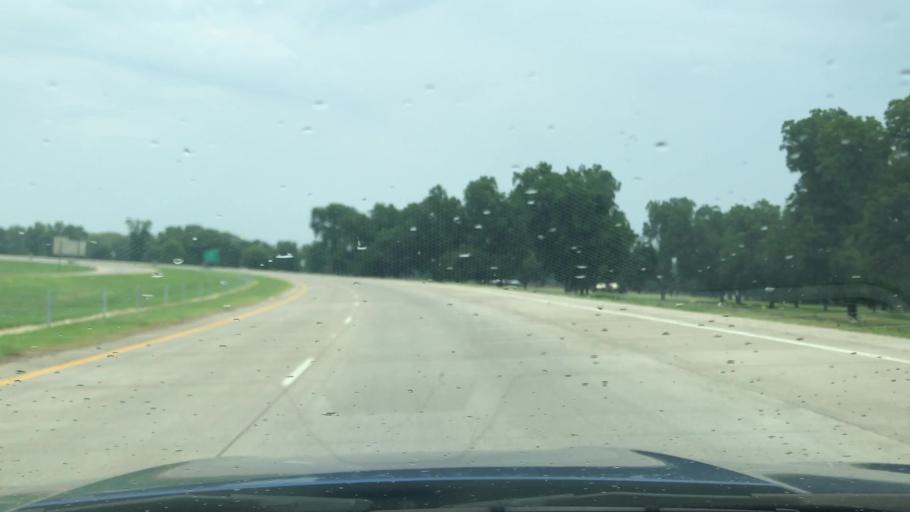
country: US
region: Louisiana
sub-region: Bossier Parish
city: Bossier City
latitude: 32.4057
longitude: -93.7146
